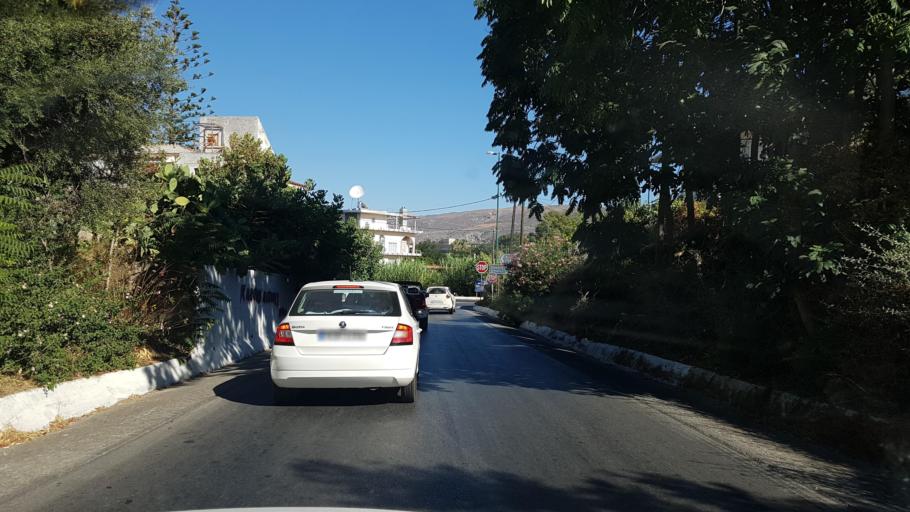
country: GR
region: Crete
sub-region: Nomos Chanias
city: Perivolia
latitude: 35.4978
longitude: 23.9923
